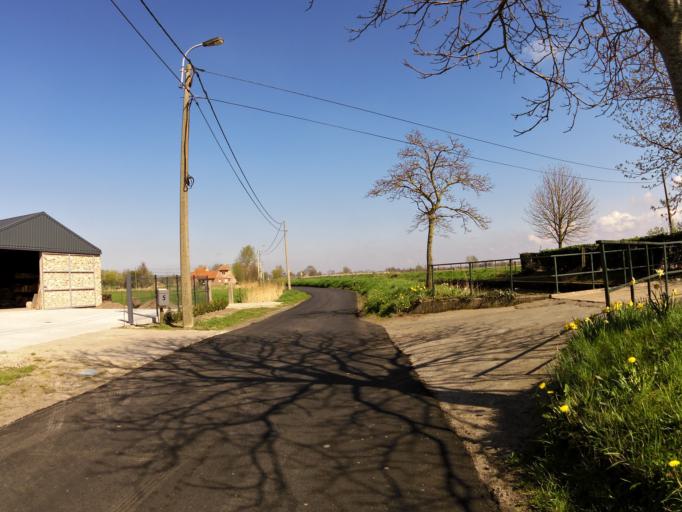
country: BE
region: Flanders
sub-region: Provincie West-Vlaanderen
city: Gistel
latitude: 51.1372
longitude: 2.9915
